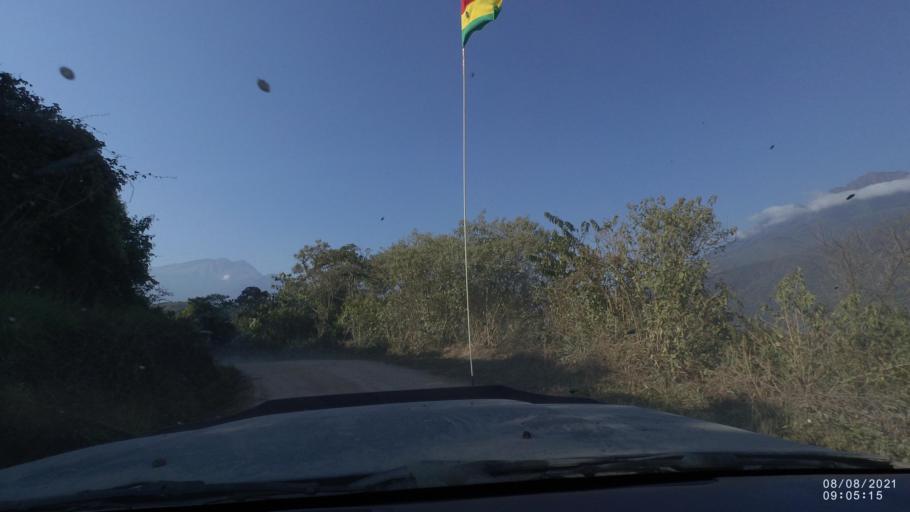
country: BO
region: La Paz
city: Quime
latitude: -16.5571
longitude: -66.7382
